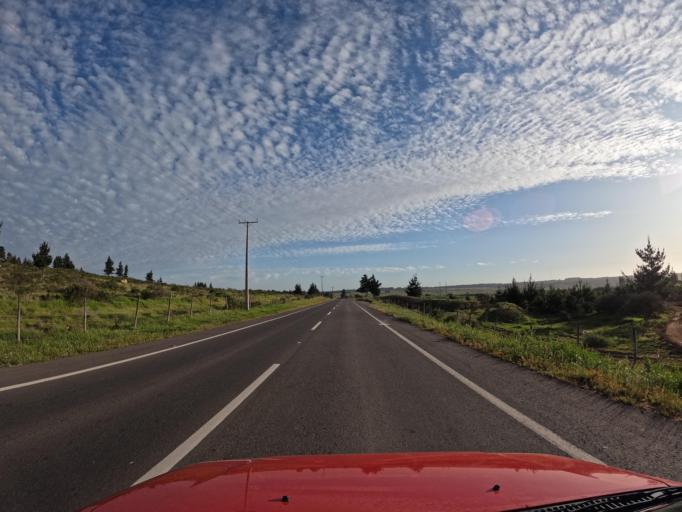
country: CL
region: Valparaiso
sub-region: San Antonio Province
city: San Antonio
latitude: -34.0538
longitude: -71.6245
